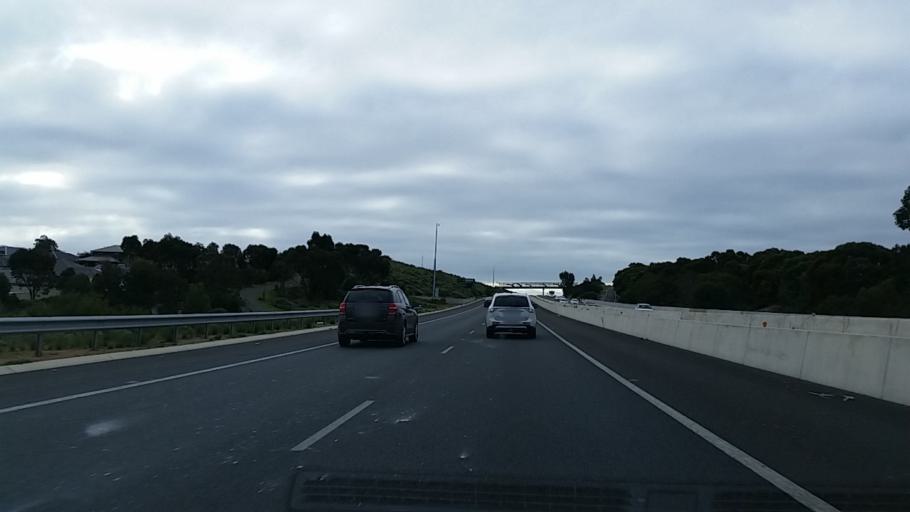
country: AU
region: South Australia
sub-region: Onkaparinga
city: Noarlunga Downs
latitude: -35.1620
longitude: 138.5075
